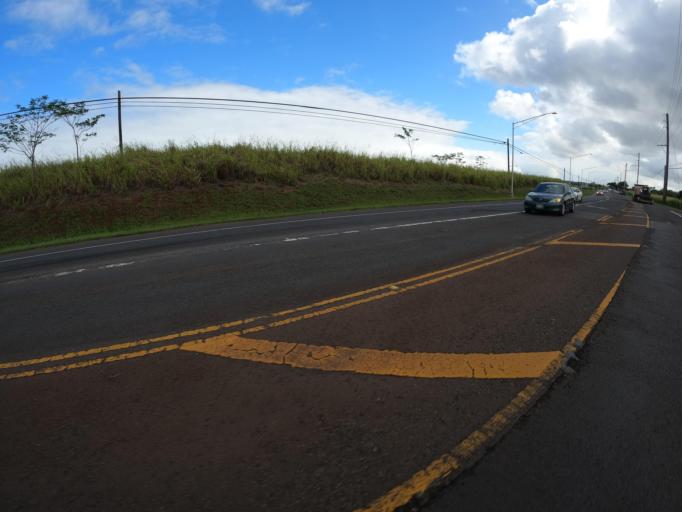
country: US
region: Hawaii
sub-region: Honolulu County
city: Whitmore Village
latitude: 21.5109
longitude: -158.0396
